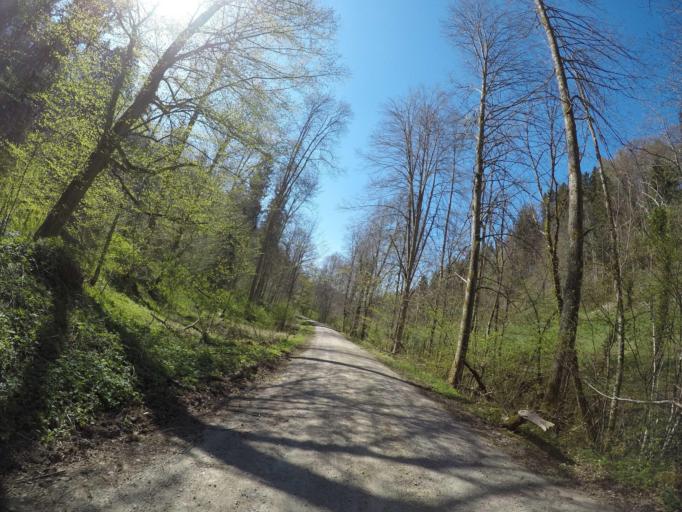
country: DE
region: Baden-Wuerttemberg
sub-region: Tuebingen Region
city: Horgenzell
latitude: 47.7978
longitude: 9.4592
